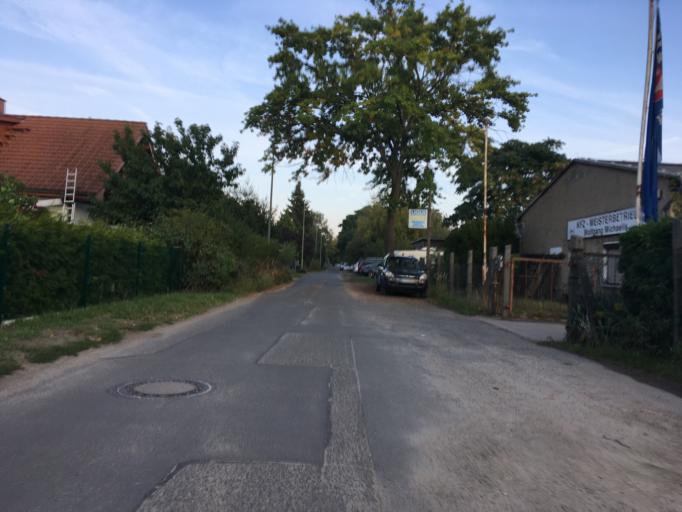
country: DE
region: Berlin
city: Biesdorf
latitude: 52.4930
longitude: 13.5497
